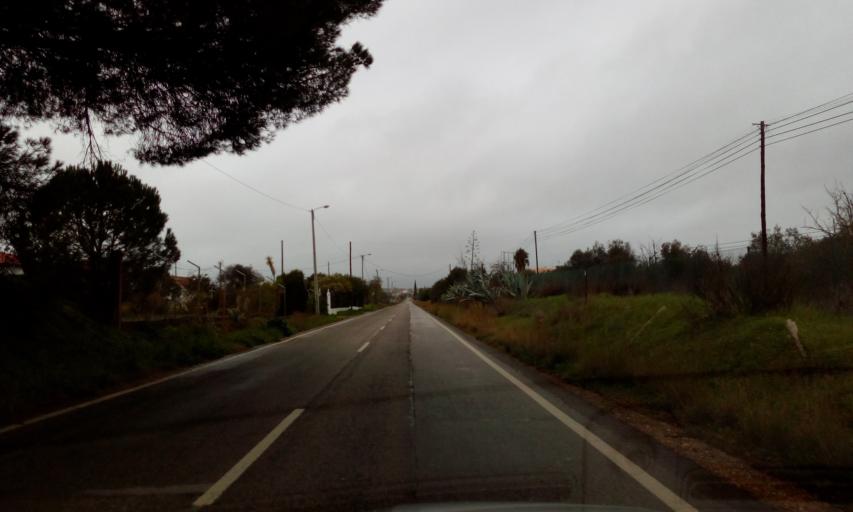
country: PT
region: Faro
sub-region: Albufeira
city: Guia
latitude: 37.1689
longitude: -8.3150
